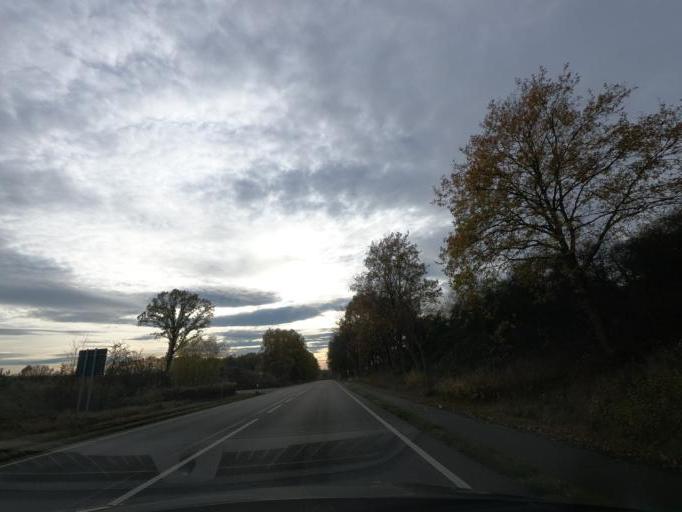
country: DE
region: Lower Saxony
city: Lehre
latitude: 52.3079
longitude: 10.6261
